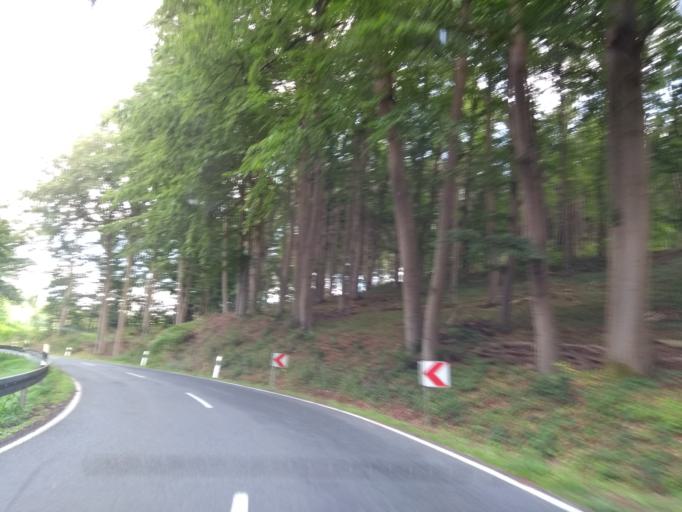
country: DE
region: Lower Saxony
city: Bad Pyrmont
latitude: 51.9756
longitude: 9.3013
